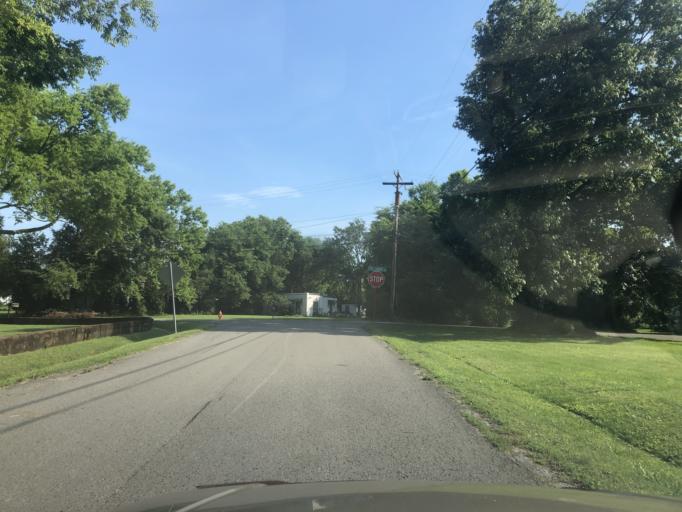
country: US
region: Tennessee
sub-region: Davidson County
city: Lakewood
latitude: 36.2287
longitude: -86.7162
